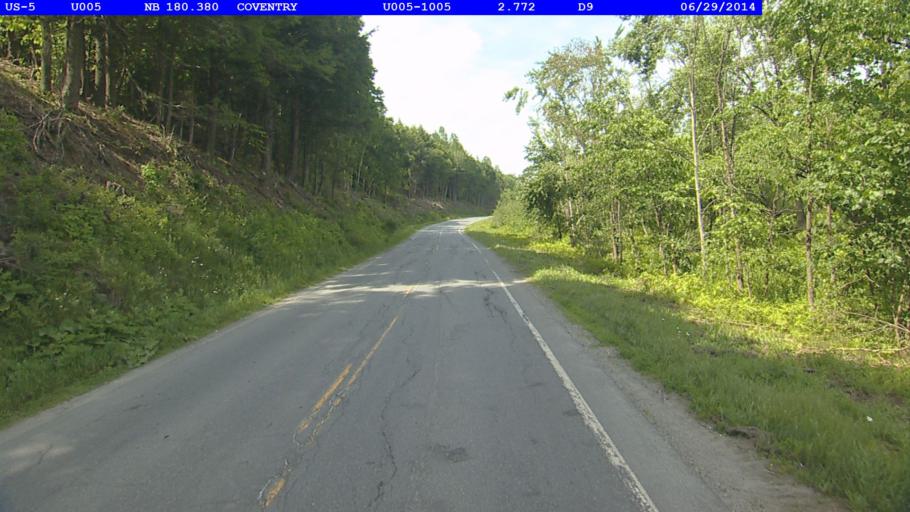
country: US
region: Vermont
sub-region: Orleans County
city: Newport
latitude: 44.8954
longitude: -72.2452
